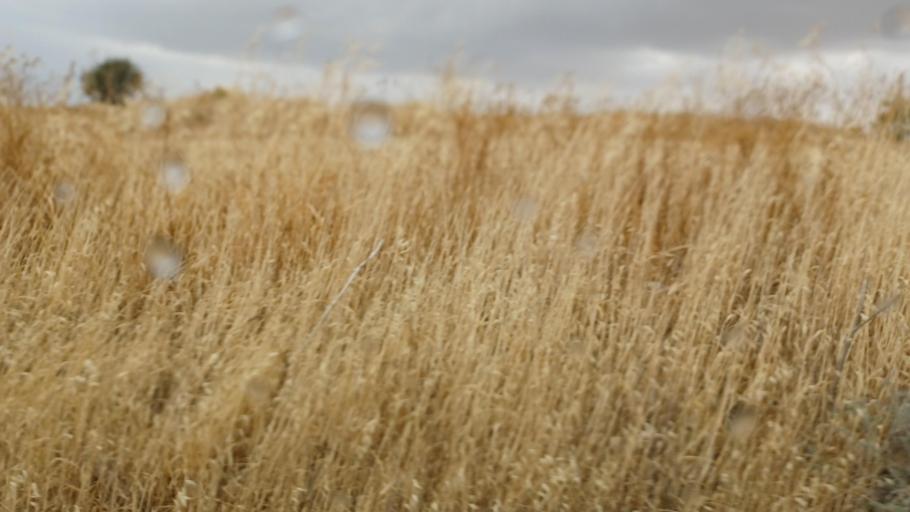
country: CY
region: Larnaka
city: Athienou
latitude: 35.0455
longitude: 33.5660
